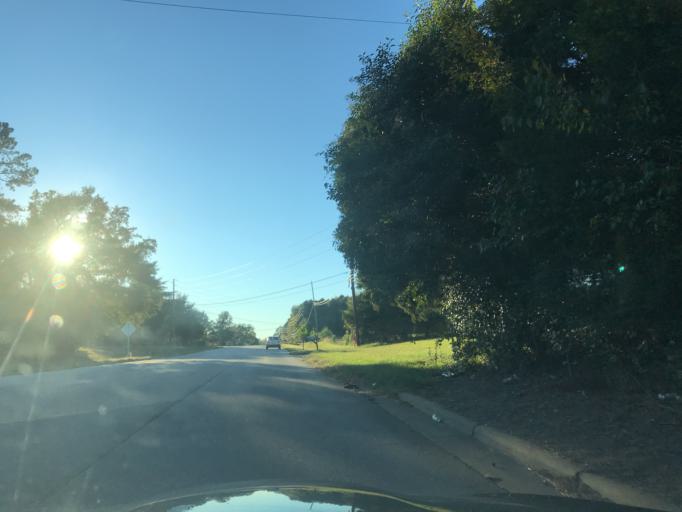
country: US
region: North Carolina
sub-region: Wake County
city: Garner
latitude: 35.7475
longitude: -78.5949
